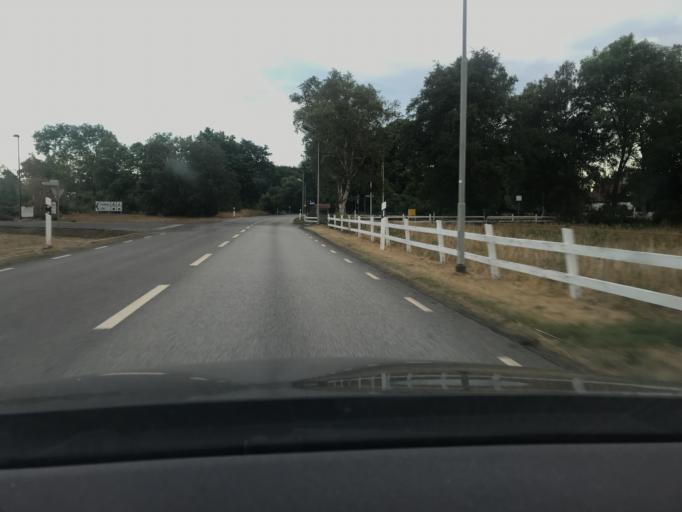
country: SE
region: Skane
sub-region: Simrishamns Kommun
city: Simrishamn
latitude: 55.5725
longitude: 14.3346
